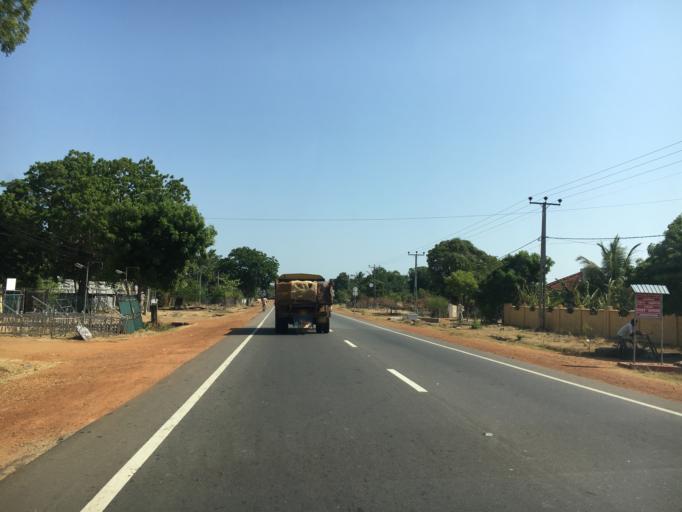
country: LK
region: Northern Province
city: Kilinochchi
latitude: 9.4310
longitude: 80.4077
